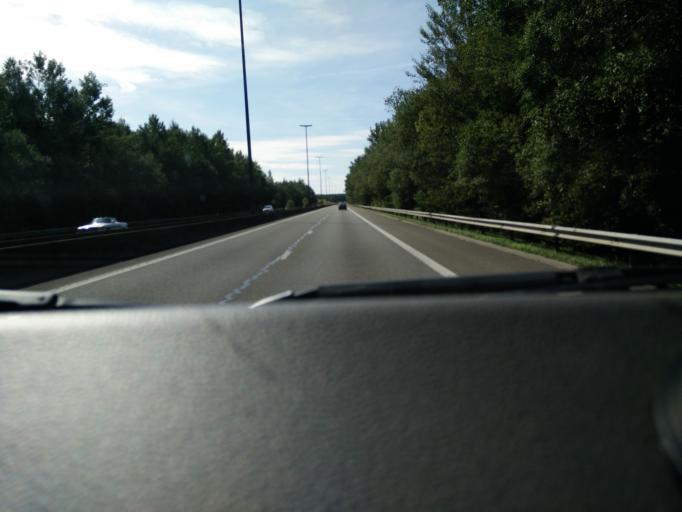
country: BE
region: Wallonia
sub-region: Province du Luxembourg
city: Libin
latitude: 49.9551
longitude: 5.2376
